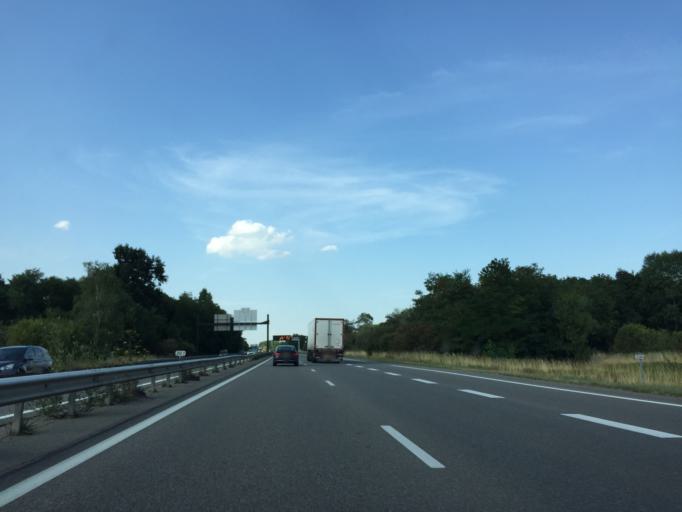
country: FR
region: Alsace
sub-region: Departement du Bas-Rhin
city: Niedernai
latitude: 48.4352
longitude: 7.4980
